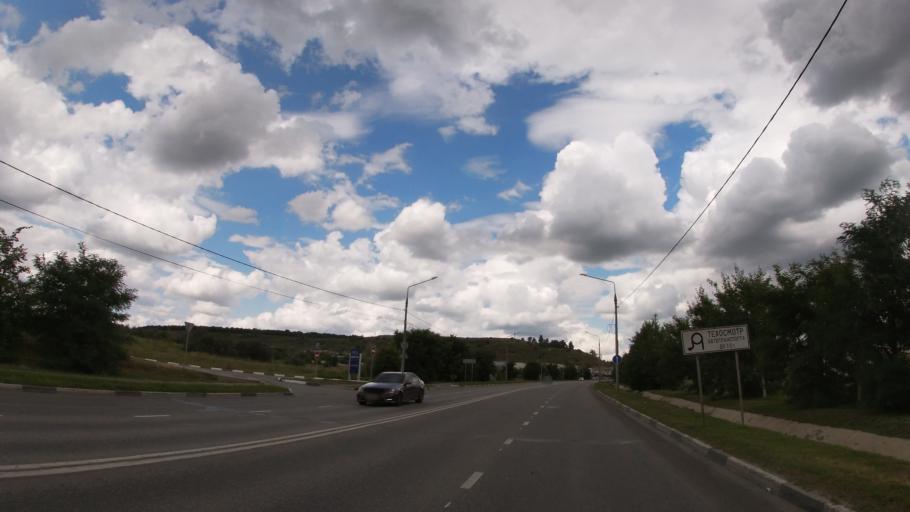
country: RU
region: Belgorod
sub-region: Belgorodskiy Rayon
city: Belgorod
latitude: 50.6121
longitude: 36.6126
